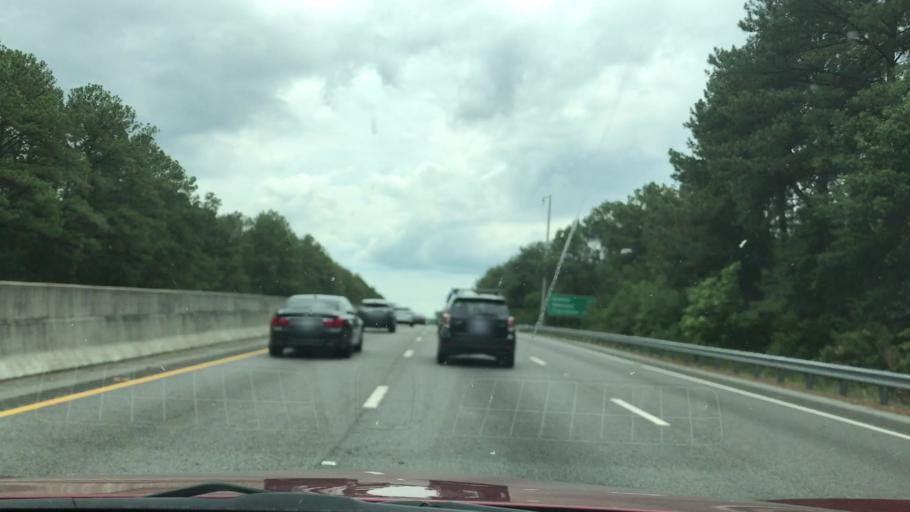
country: US
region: South Carolina
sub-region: Lexington County
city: Springdale
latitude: 33.9473
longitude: -81.0904
